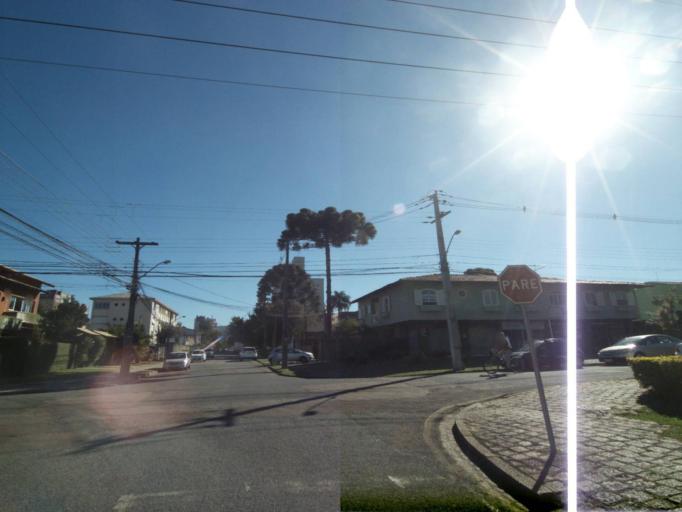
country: BR
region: Parana
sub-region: Curitiba
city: Curitiba
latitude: -25.4197
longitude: -49.2515
